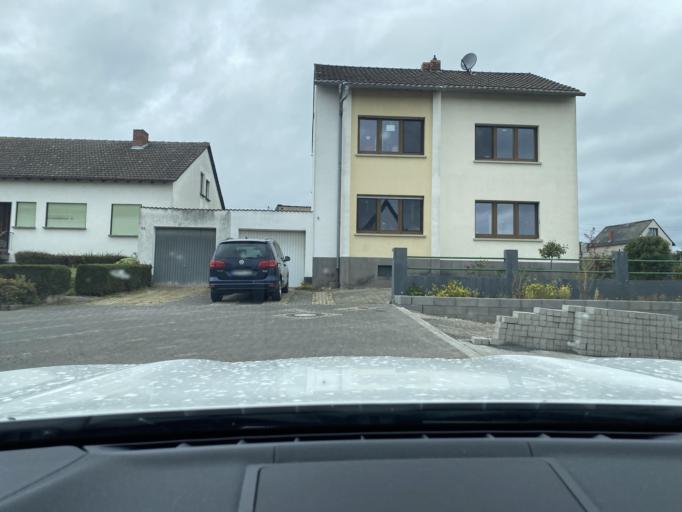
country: DE
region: Rheinland-Pfalz
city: Plaidt
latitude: 50.3980
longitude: 7.4082
